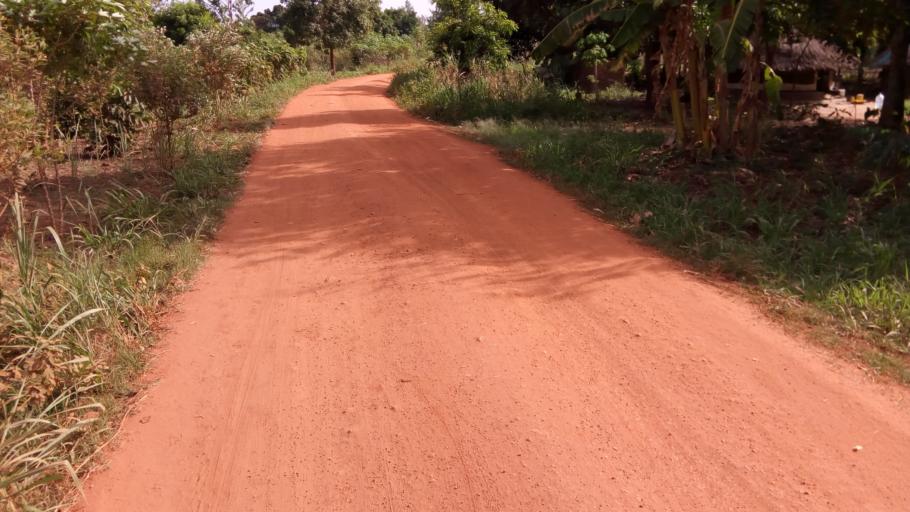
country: UG
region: Northern Region
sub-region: Gulu District
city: Gulu
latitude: 2.8022
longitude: 32.3227
